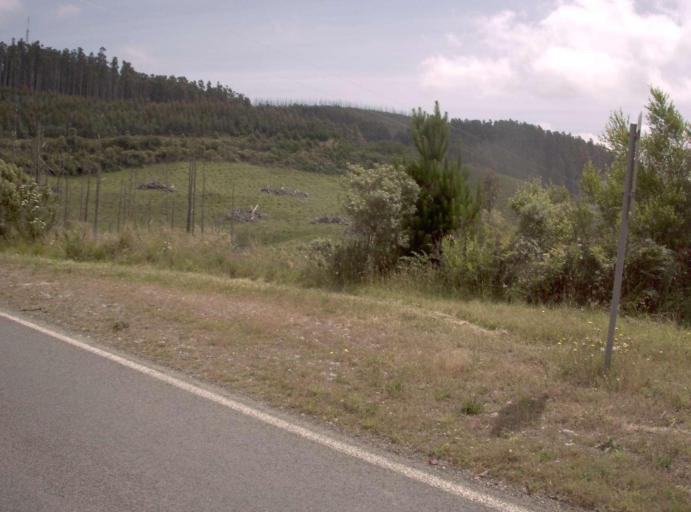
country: AU
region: Victoria
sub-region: Latrobe
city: Traralgon
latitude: -38.3836
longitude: 146.5665
